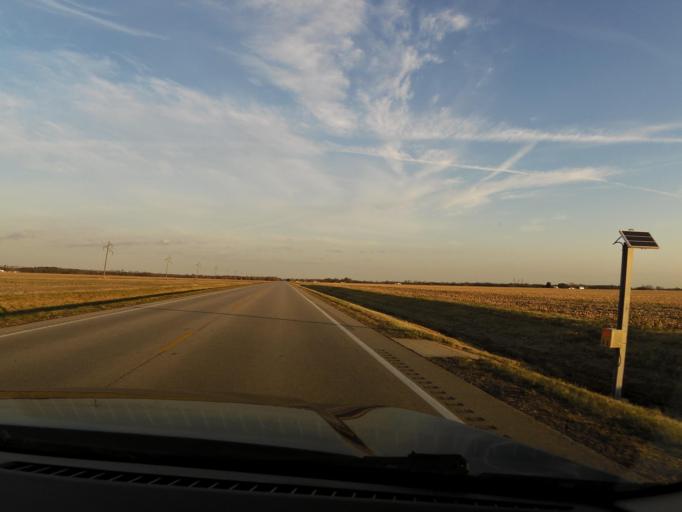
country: US
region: Illinois
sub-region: Fayette County
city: Vandalia
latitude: 38.8288
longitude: -89.0880
